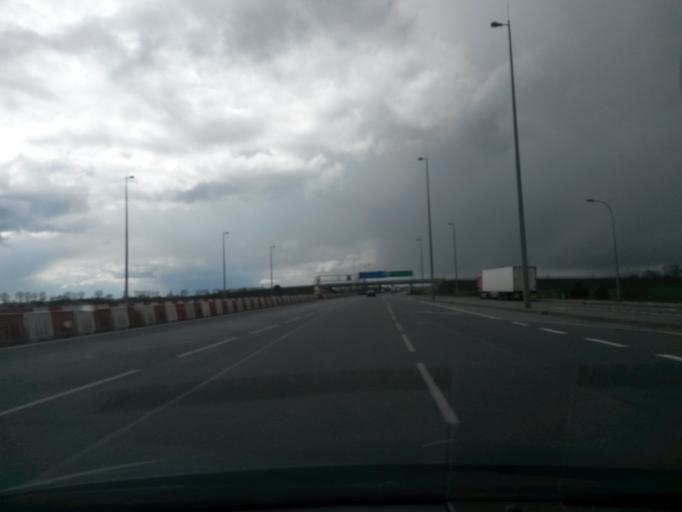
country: PL
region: Greater Poland Voivodeship
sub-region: Powiat poznanski
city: Kleszczewo
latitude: 52.3115
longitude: 17.1489
